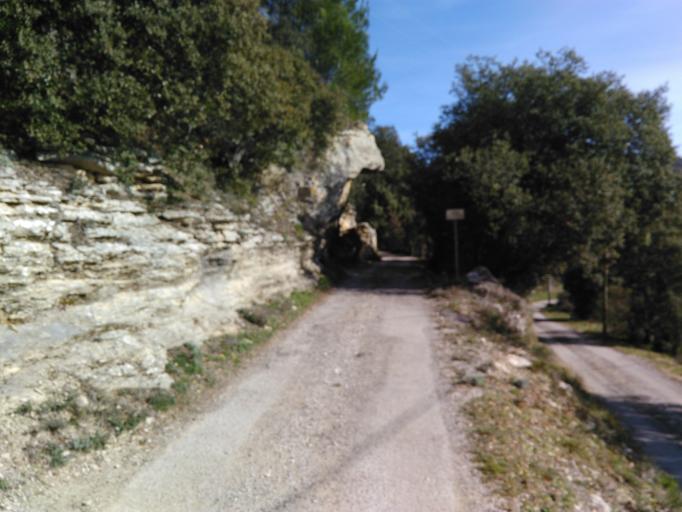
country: FR
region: Provence-Alpes-Cote d'Azur
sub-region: Departement du Vaucluse
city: Venasque
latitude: 43.9738
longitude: 5.1486
